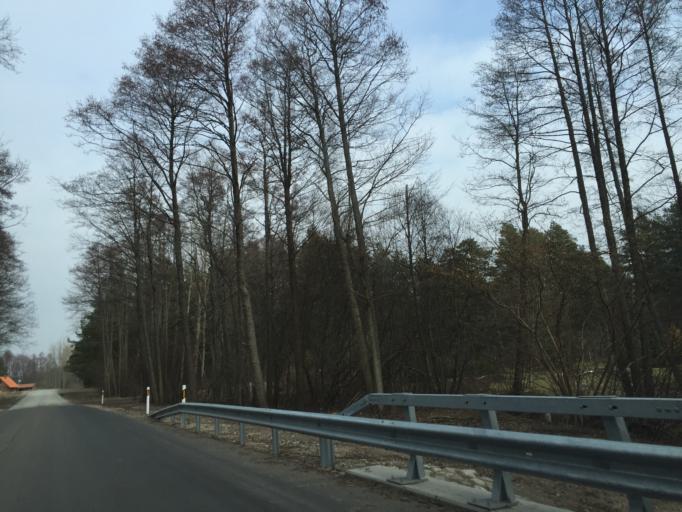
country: LV
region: Salacgrivas
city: Ainazi
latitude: 57.9514
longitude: 24.3936
